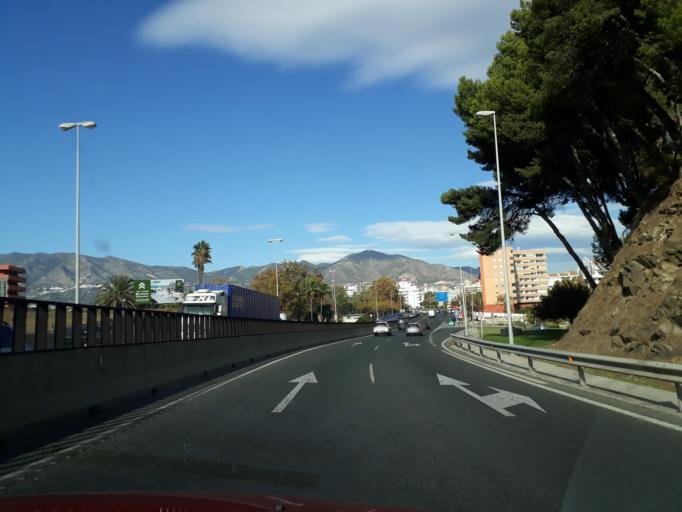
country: ES
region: Andalusia
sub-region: Provincia de Malaga
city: Fuengirola
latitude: 36.5256
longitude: -4.6302
